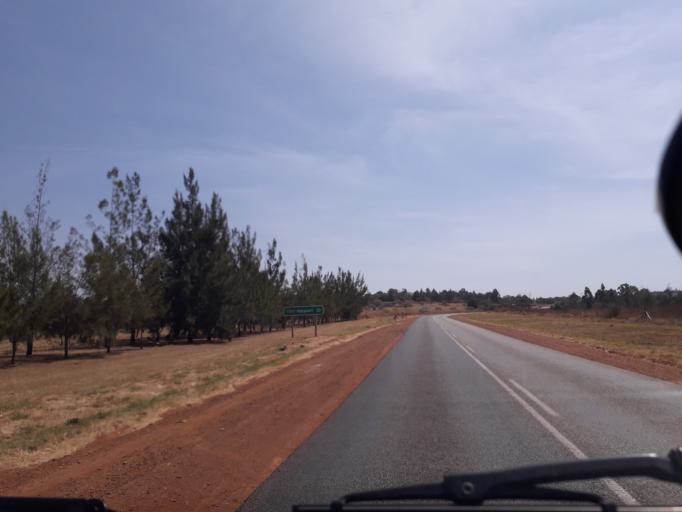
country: ZA
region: Gauteng
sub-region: West Rand District Municipality
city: Krugersdorp
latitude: -26.0024
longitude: 27.7037
